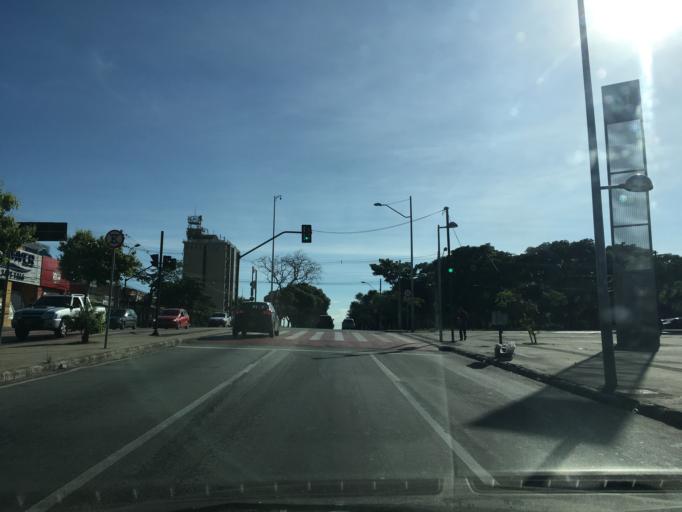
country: BR
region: Minas Gerais
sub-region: Belo Horizonte
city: Belo Horizonte
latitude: -19.8632
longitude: -43.9709
